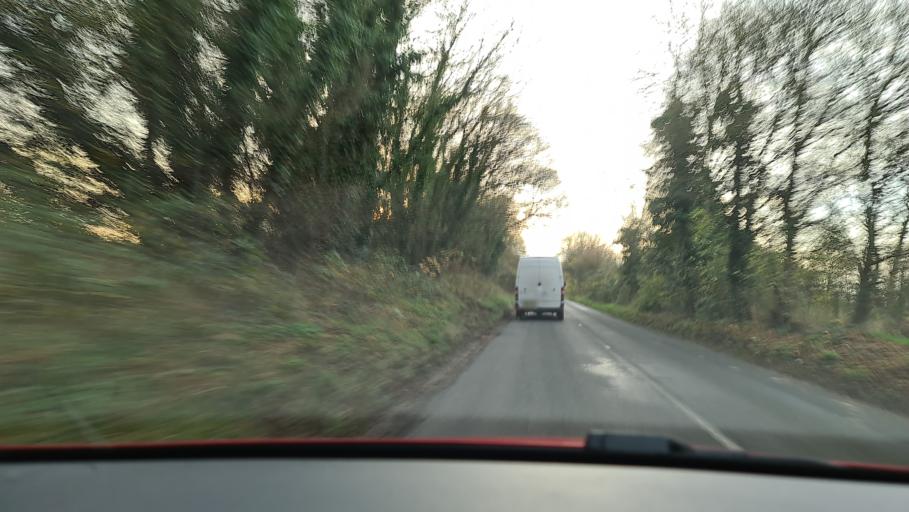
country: GB
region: England
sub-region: Oxfordshire
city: Kidlington
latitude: 51.8478
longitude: -1.2535
